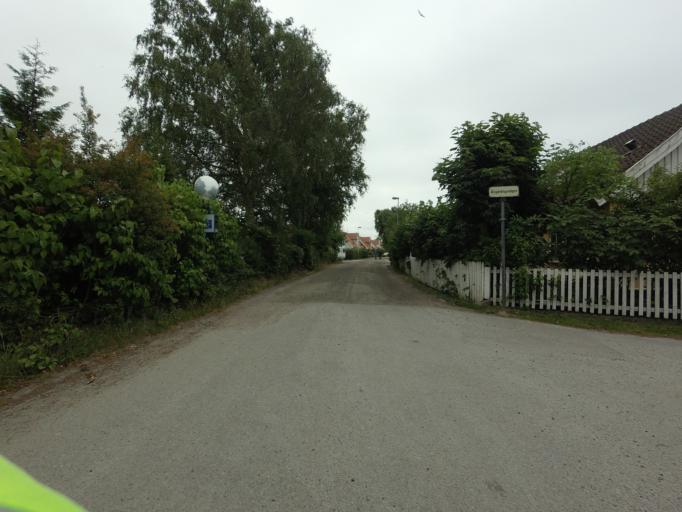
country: SE
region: Skane
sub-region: Malmo
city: Bunkeflostrand
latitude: 55.5298
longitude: 12.9255
